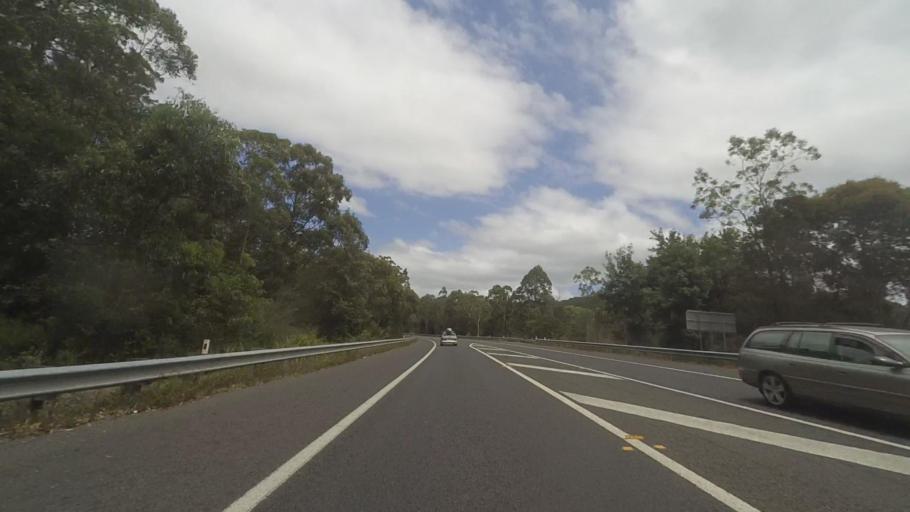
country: AU
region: New South Wales
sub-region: Shoalhaven Shire
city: Milton
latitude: -35.2325
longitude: 150.4322
